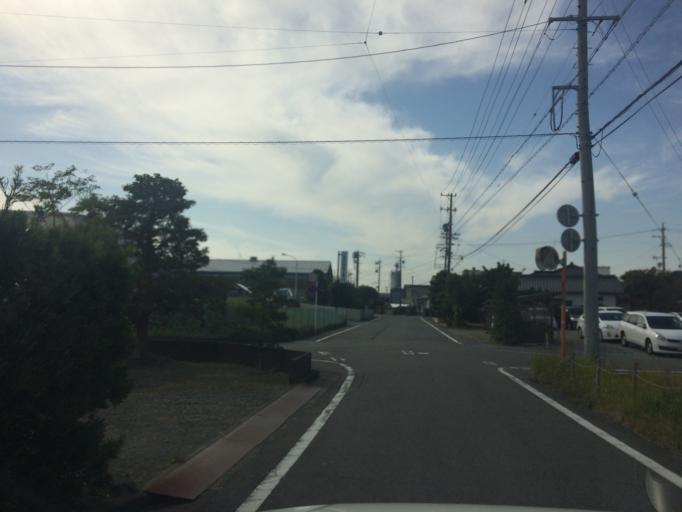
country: JP
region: Shizuoka
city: Yaizu
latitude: 34.8054
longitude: 138.3041
